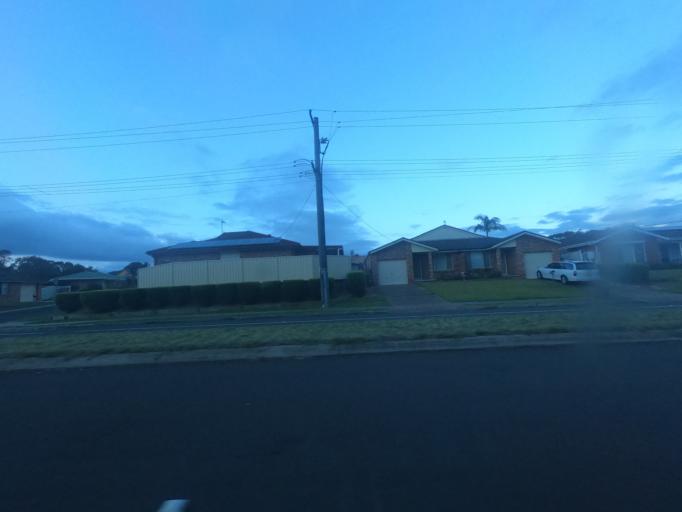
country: AU
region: New South Wales
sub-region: Wollongong
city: Koonawarra
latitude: -34.5014
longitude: 150.8015
